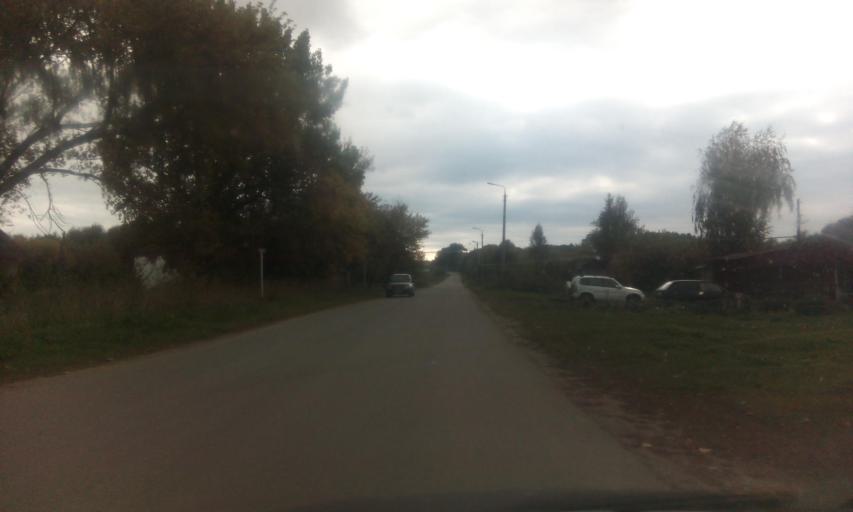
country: RU
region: Tula
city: Gritsovskiy
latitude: 54.1147
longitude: 38.1657
